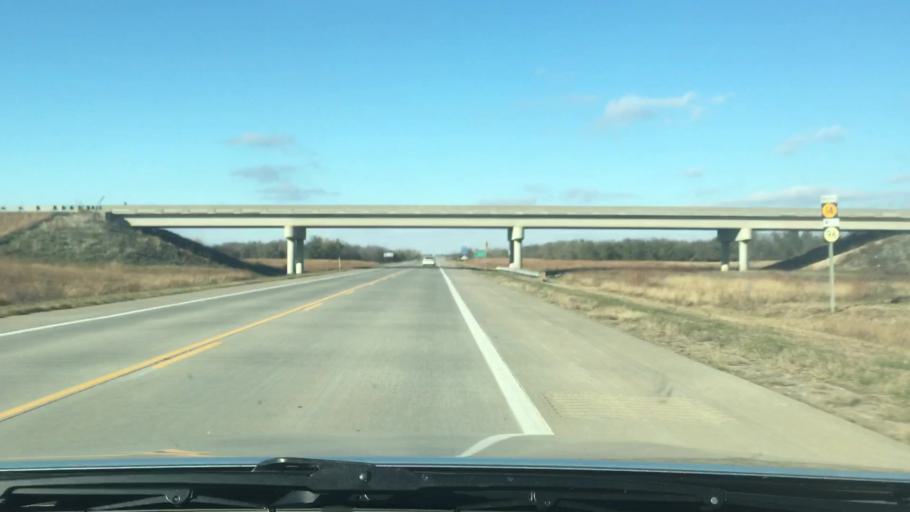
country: US
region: Kansas
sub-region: Reno County
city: South Hutchinson
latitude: 38.0418
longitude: -97.9857
